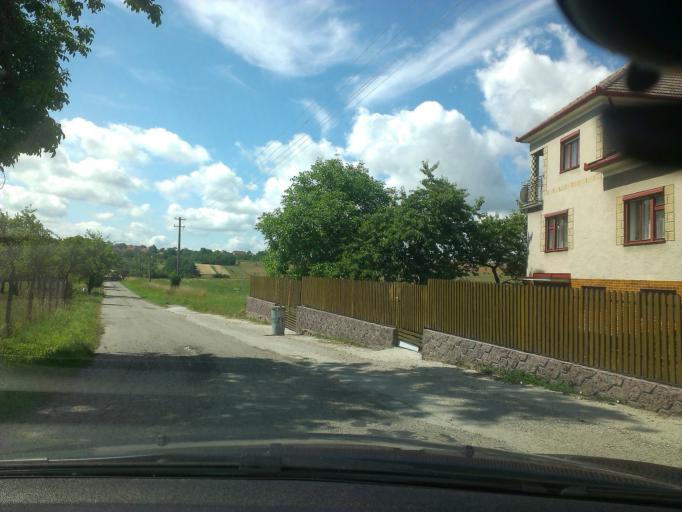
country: SK
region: Trenciansky
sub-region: Okres Myjava
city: Myjava
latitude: 48.7793
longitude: 17.5907
